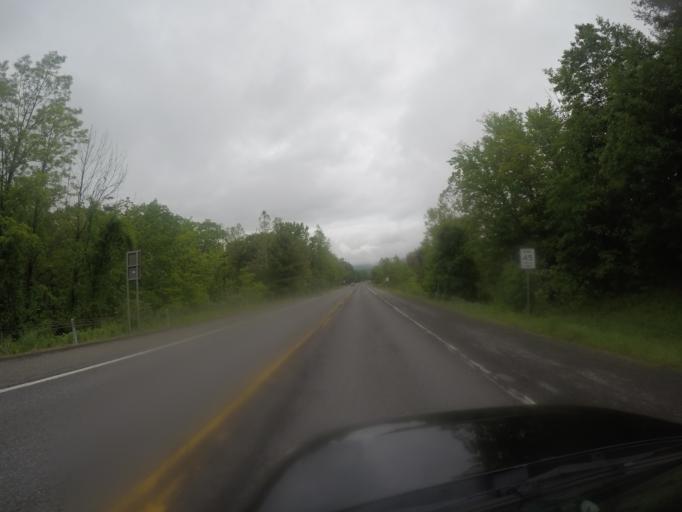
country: US
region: New York
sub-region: Ulster County
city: Shokan
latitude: 42.0140
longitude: -74.2698
